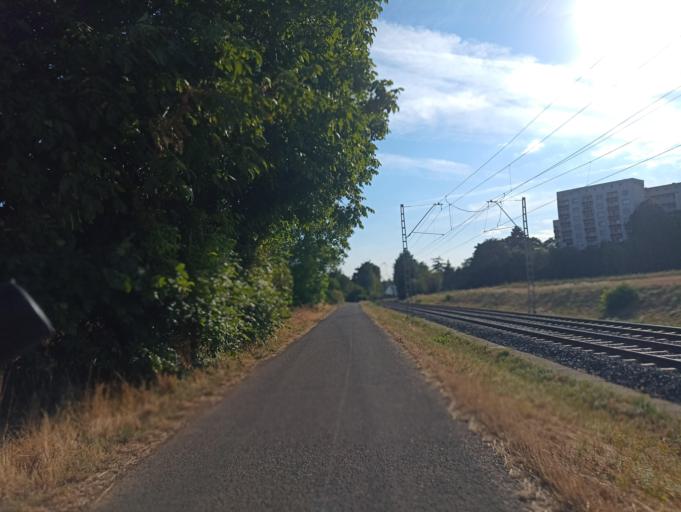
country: DE
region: Hesse
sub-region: Regierungsbezirk Darmstadt
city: Bad Homburg vor der Hoehe
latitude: 50.1878
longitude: 8.6698
